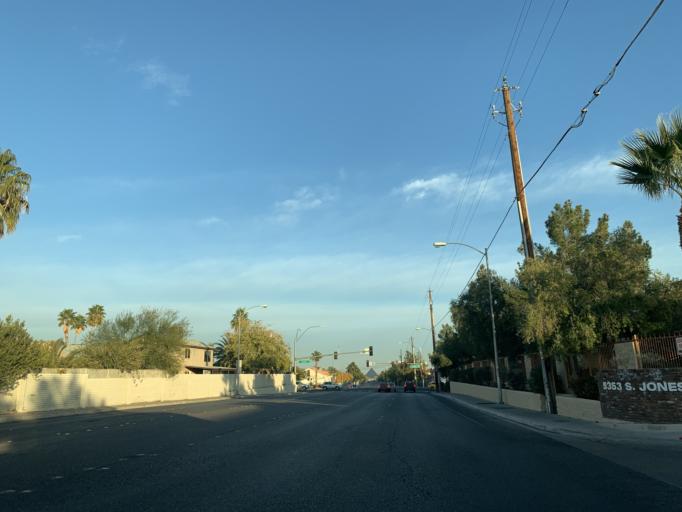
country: US
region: Nevada
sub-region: Clark County
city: Spring Valley
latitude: 36.0925
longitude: -115.2263
